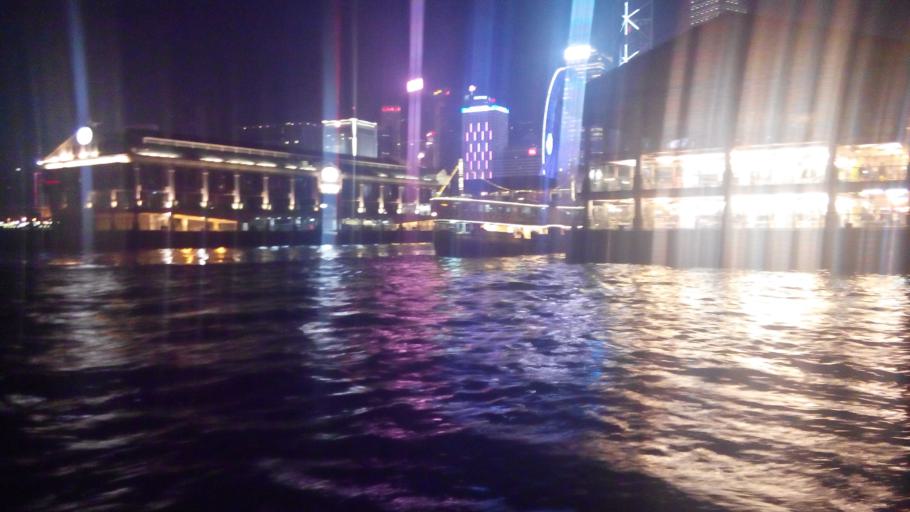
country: HK
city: Hong Kong
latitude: 22.2876
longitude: 114.1614
